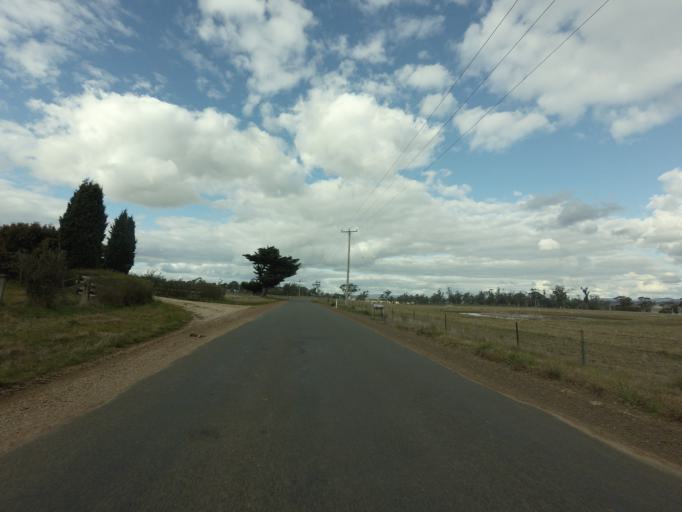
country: AU
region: Tasmania
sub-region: Northern Midlands
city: Longford
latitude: -41.8060
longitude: 147.1563
